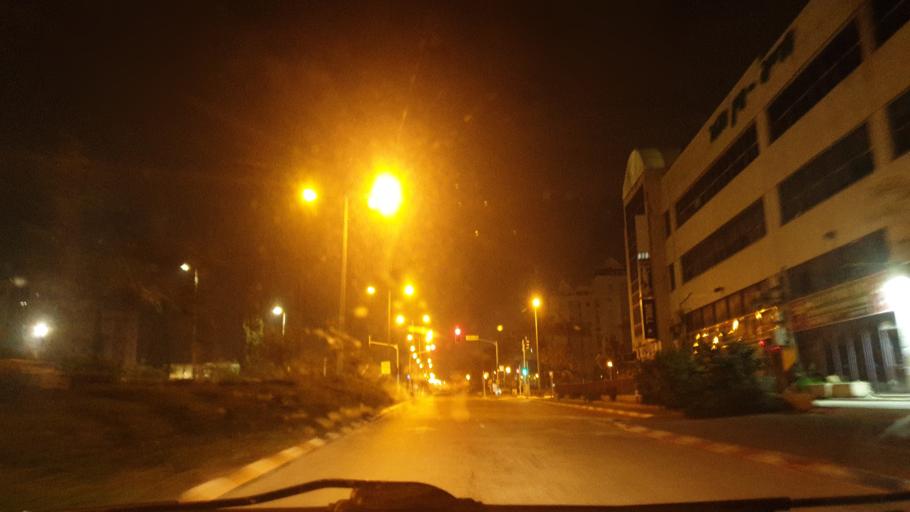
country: IL
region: Central District
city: Bet Dagan
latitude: 31.9755
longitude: 34.8129
